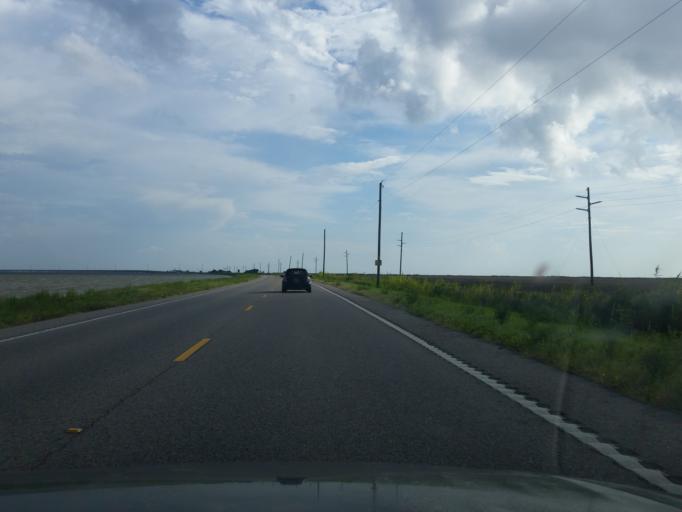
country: US
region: Alabama
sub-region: Mobile County
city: Dauphin Island
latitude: 30.3265
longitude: -88.1351
